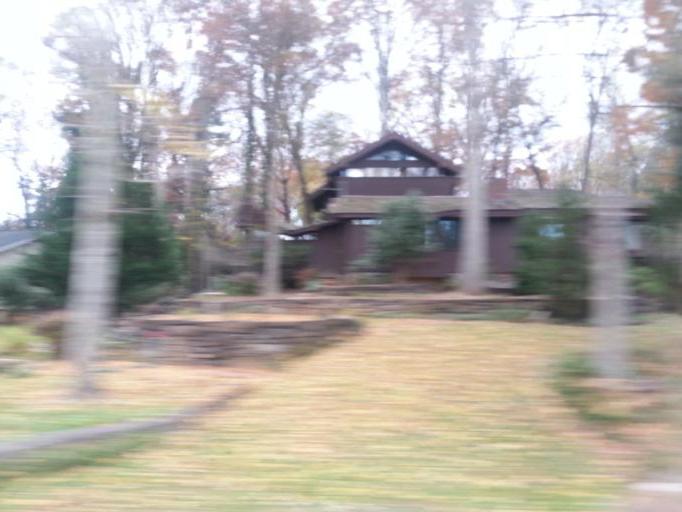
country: US
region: Tennessee
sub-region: Knox County
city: Knoxville
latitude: 35.9469
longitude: -84.0026
